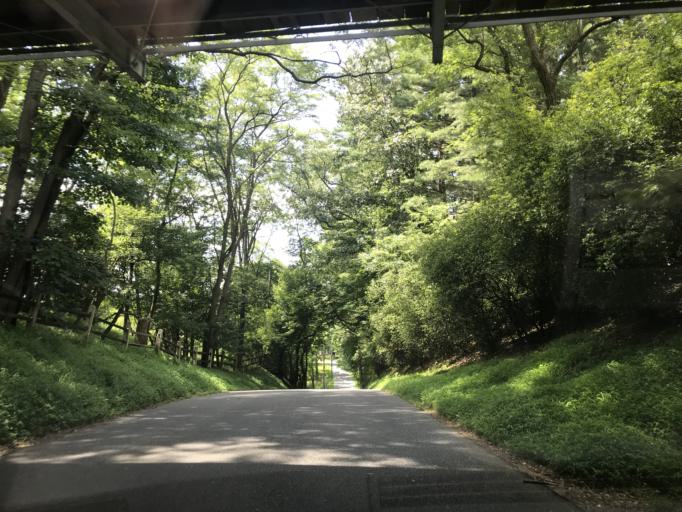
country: US
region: Delaware
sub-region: New Castle County
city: Hockessin
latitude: 39.7879
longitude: -75.6532
